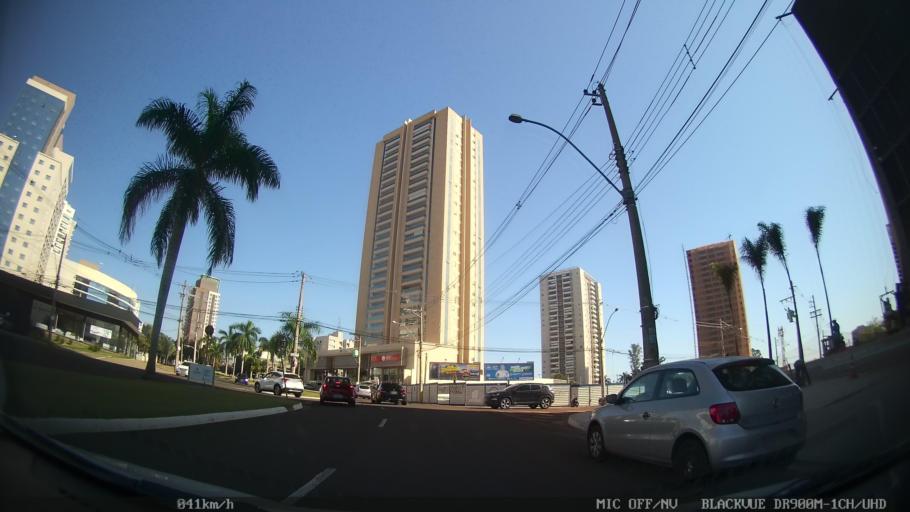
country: BR
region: Sao Paulo
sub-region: Ribeirao Preto
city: Ribeirao Preto
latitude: -21.2099
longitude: -47.7983
